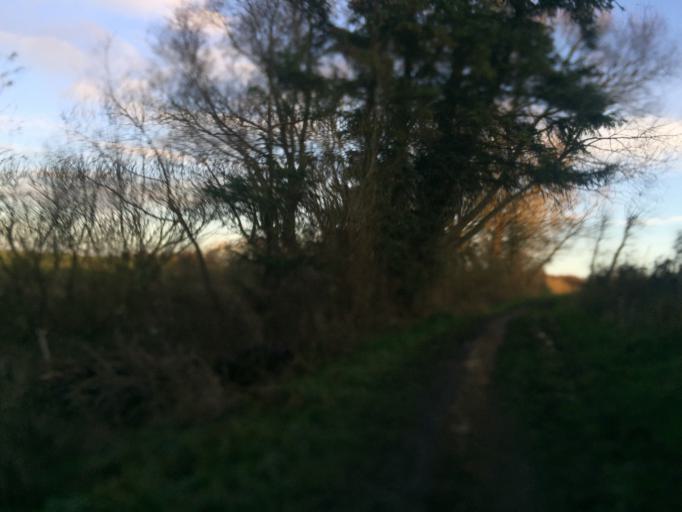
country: DK
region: Zealand
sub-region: Ringsted Kommune
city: Ringsted
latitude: 55.4269
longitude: 11.7750
